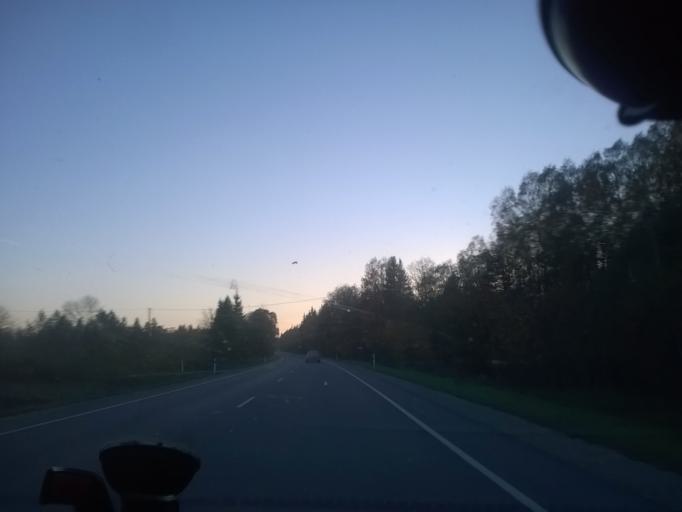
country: EE
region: Harju
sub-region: Nissi vald
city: Turba
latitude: 58.9915
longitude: 24.0247
